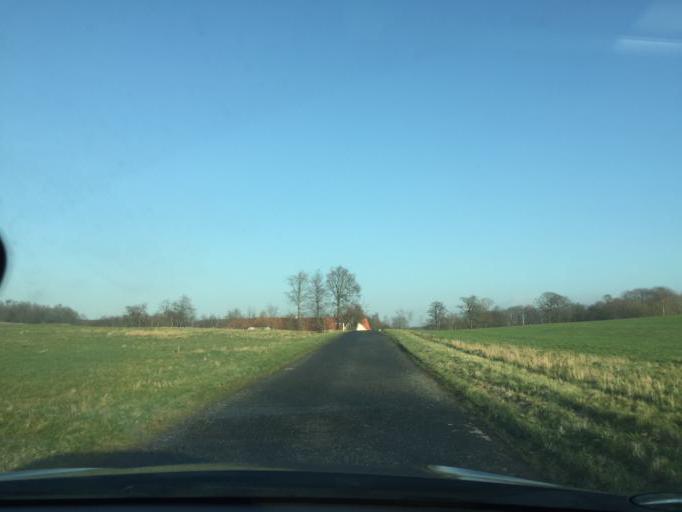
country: DK
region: South Denmark
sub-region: Faaborg-Midtfyn Kommune
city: Faaborg
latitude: 55.1358
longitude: 10.2491
